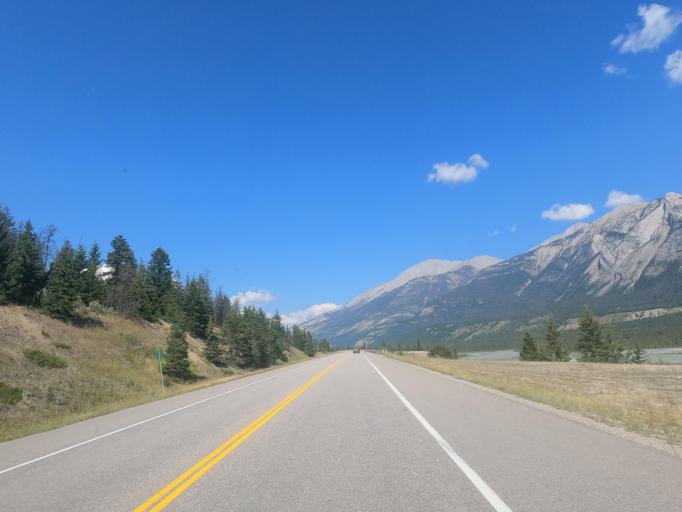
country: CA
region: Alberta
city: Jasper Park Lodge
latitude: 52.9435
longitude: -118.0394
